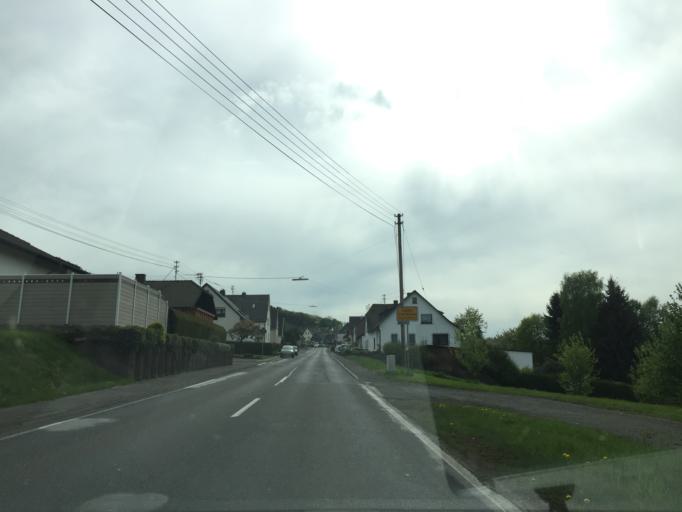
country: DE
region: Rheinland-Pfalz
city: Langenbach bei Marienberg
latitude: 50.6348
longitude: 7.9442
